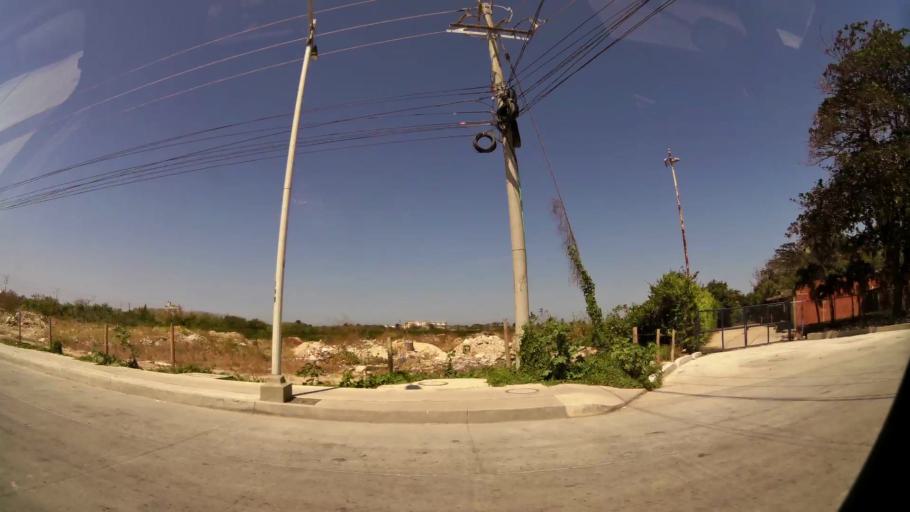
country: CO
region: Atlantico
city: Barranquilla
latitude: 10.9739
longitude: -74.7673
